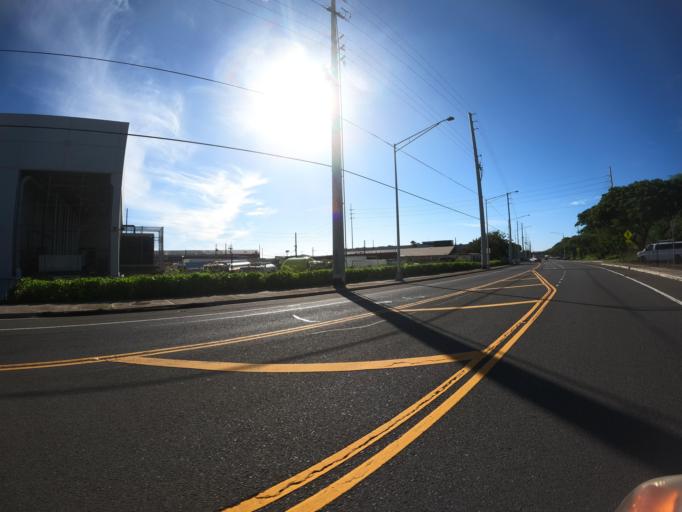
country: US
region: Hawaii
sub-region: Honolulu County
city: Halawa Heights
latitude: 21.3405
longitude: -157.9014
